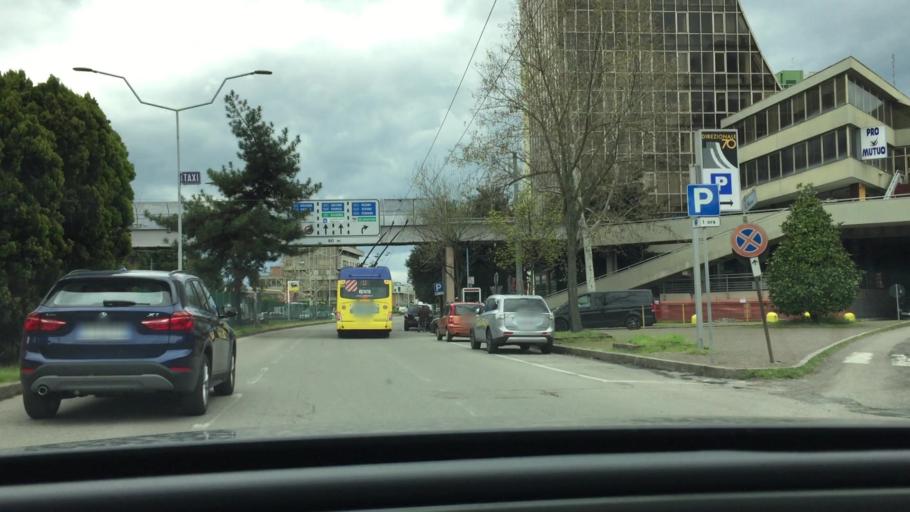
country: IT
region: Emilia-Romagna
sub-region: Provincia di Modena
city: Modena
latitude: 44.6363
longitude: 10.9045
